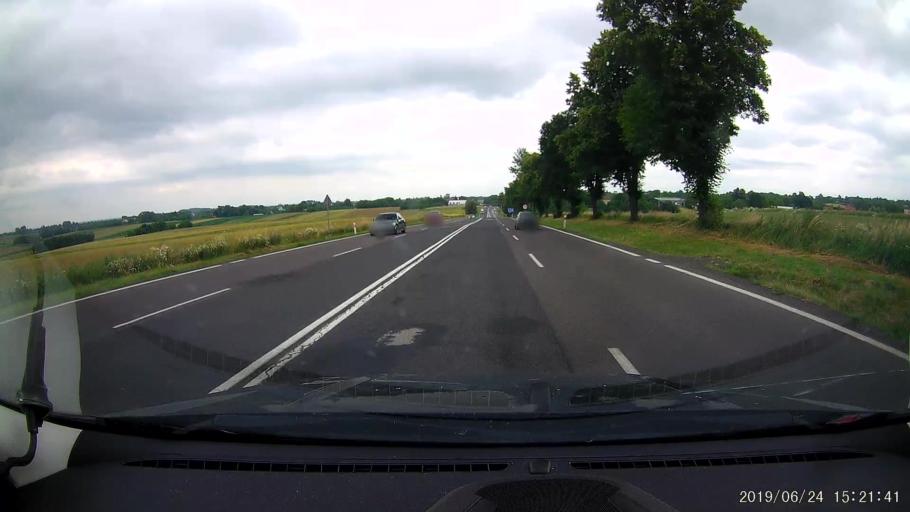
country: PL
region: Subcarpathian Voivodeship
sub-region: Powiat jaroslawski
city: Wierzbna
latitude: 50.0346
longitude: 22.5895
